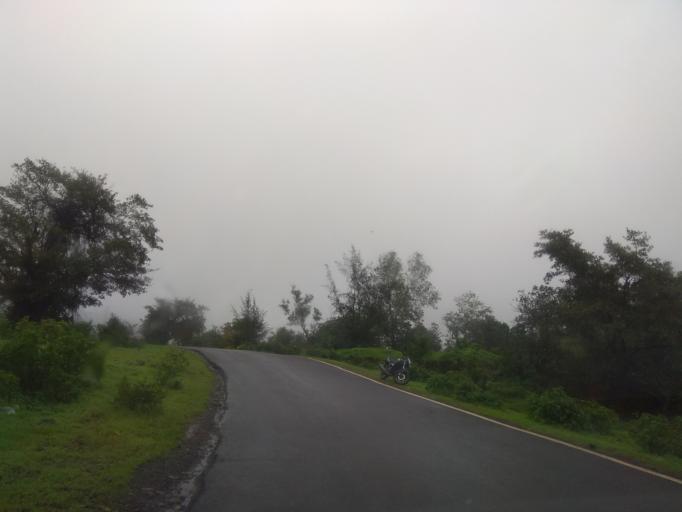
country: IN
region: Maharashtra
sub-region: Raigarh
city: Indapur
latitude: 18.4902
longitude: 73.4261
